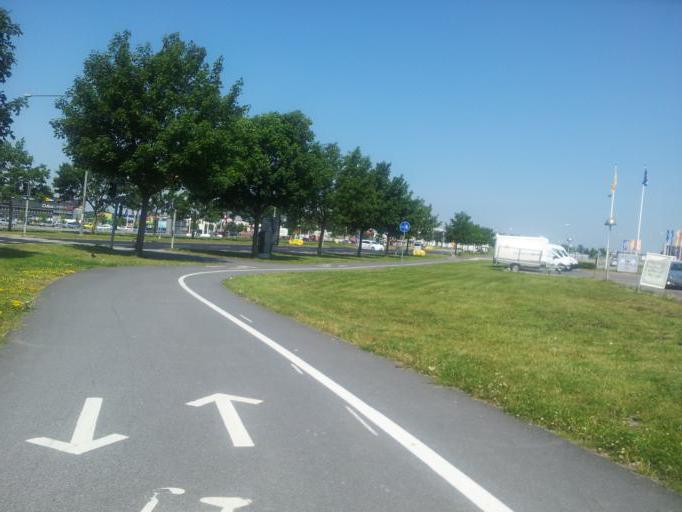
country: SE
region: Uppsala
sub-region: Uppsala Kommun
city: Saevja
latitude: 59.8454
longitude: 17.6907
